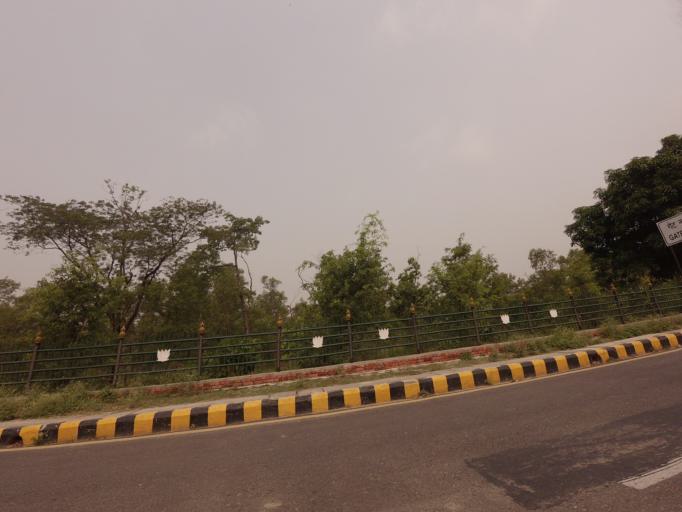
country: IN
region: Uttar Pradesh
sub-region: Maharajganj
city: Nautanwa
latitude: 27.4825
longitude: 83.2841
